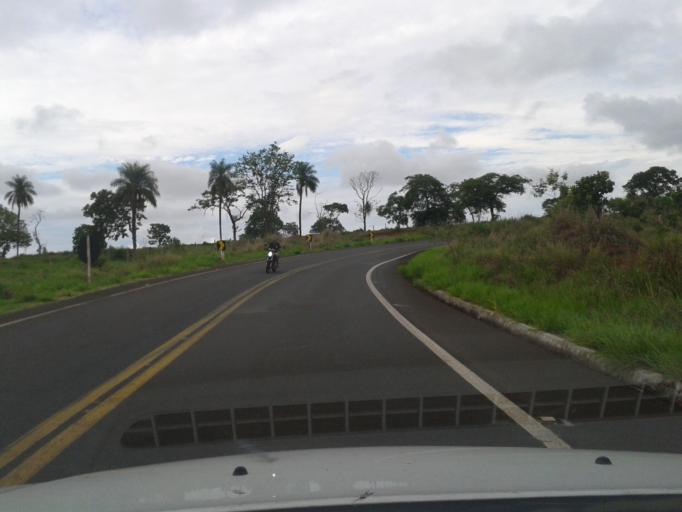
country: BR
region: Minas Gerais
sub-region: Campina Verde
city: Campina Verde
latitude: -19.5214
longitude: -49.7186
